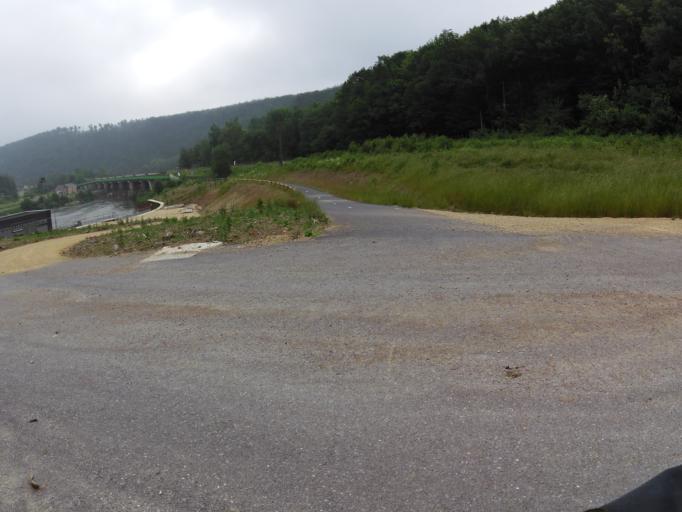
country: FR
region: Champagne-Ardenne
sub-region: Departement des Ardennes
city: Fumay
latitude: 49.9779
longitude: 4.6807
